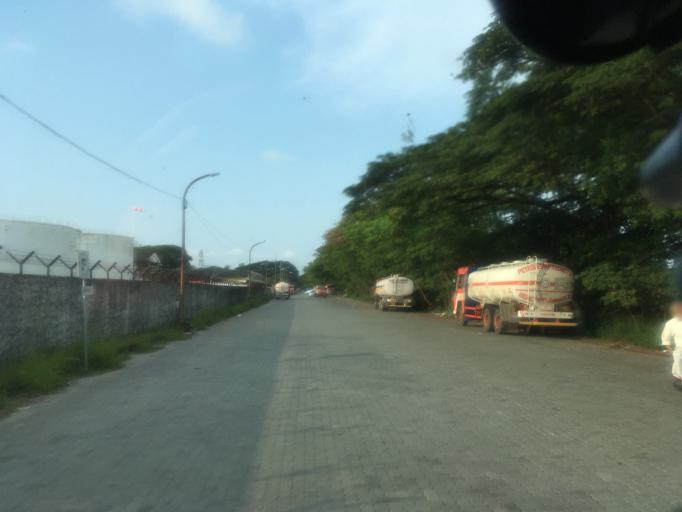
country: IN
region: Kerala
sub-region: Ernakulam
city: Cochin
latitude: 9.9496
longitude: 76.2684
